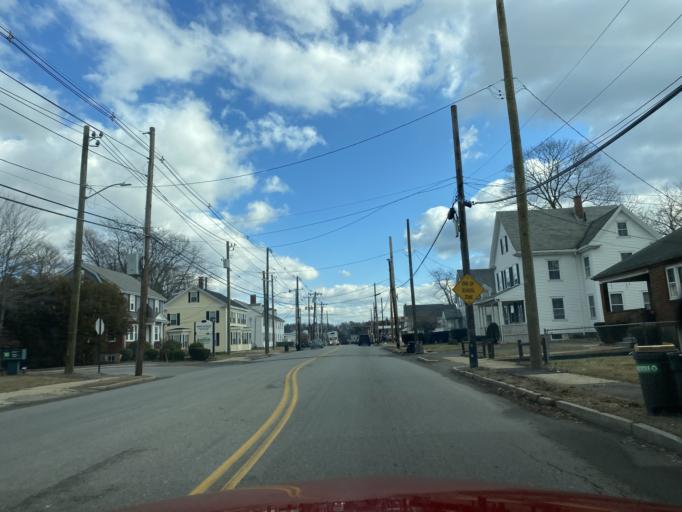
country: US
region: Massachusetts
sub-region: Middlesex County
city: Stoneham
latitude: 42.4798
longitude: -71.1236
